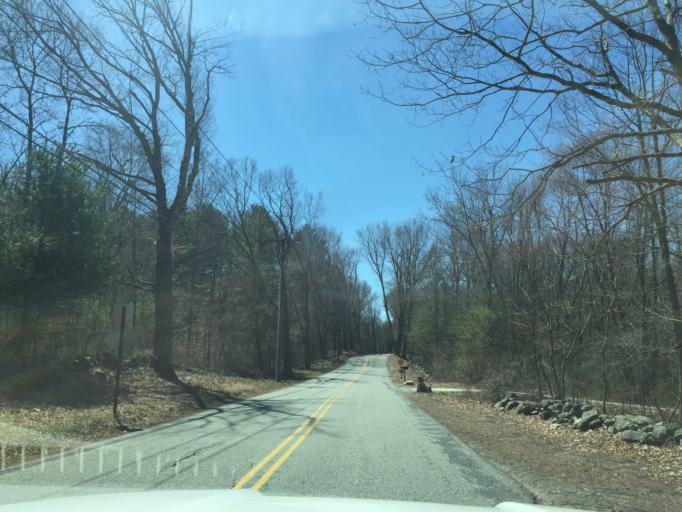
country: US
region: Connecticut
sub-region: Windham County
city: Quinebaug
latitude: 42.0062
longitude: -71.9485
